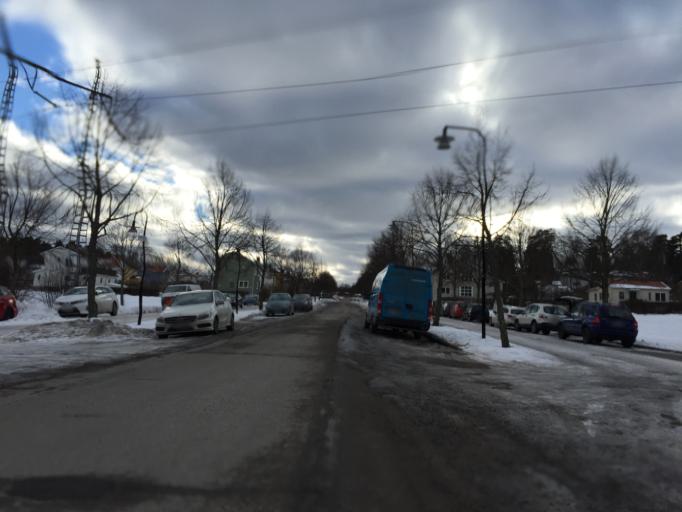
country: SE
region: Stockholm
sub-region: Stockholms Kommun
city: Bromma
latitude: 59.3547
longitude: 17.9014
